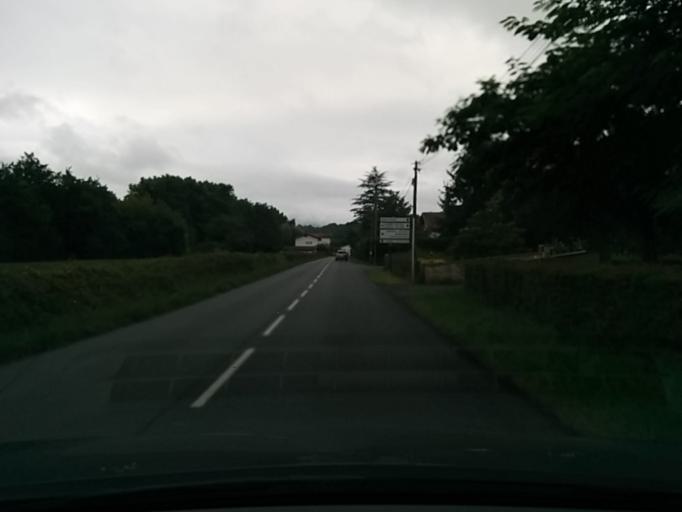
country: FR
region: Aquitaine
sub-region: Departement des Pyrenees-Atlantiques
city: Saint-Pee-sur-Nivelle
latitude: 43.3243
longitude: -1.5491
